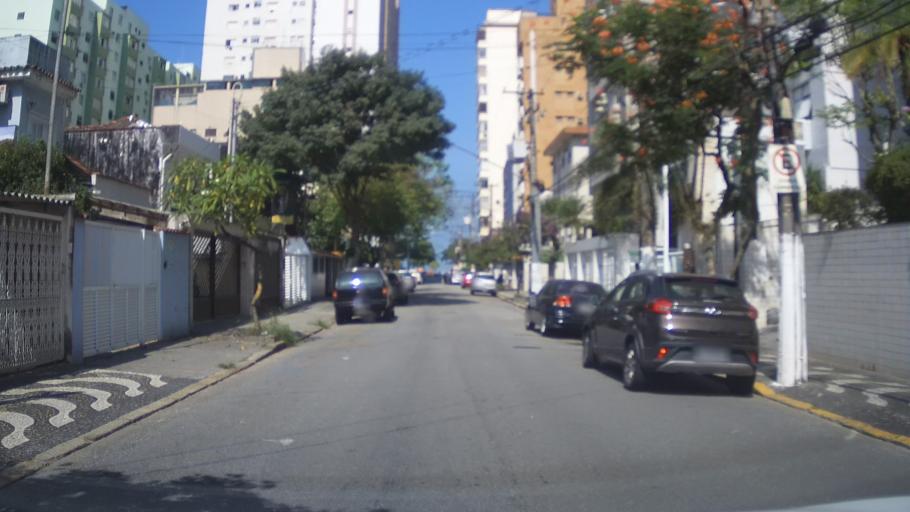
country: BR
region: Sao Paulo
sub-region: Santos
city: Santos
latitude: -23.9812
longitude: -46.3092
